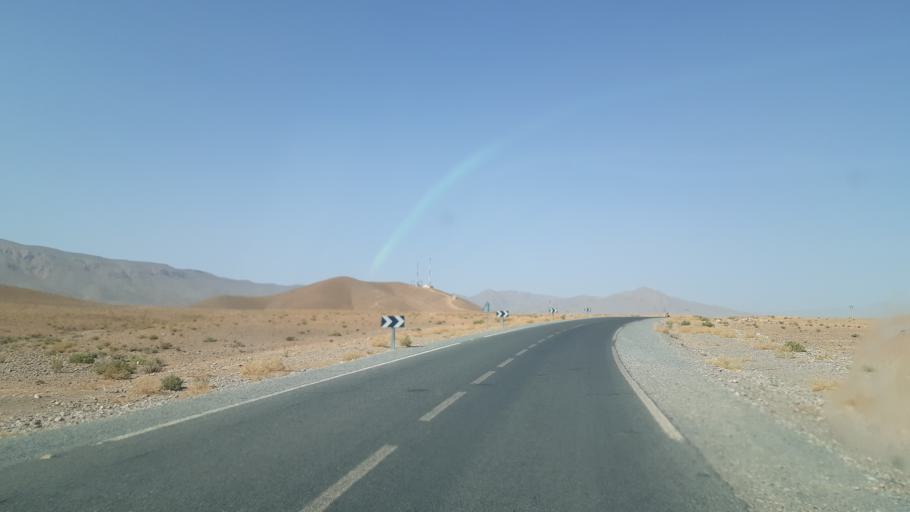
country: MA
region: Meknes-Tafilalet
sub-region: Errachidia
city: Amouguer
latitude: 32.2468
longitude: -4.5845
